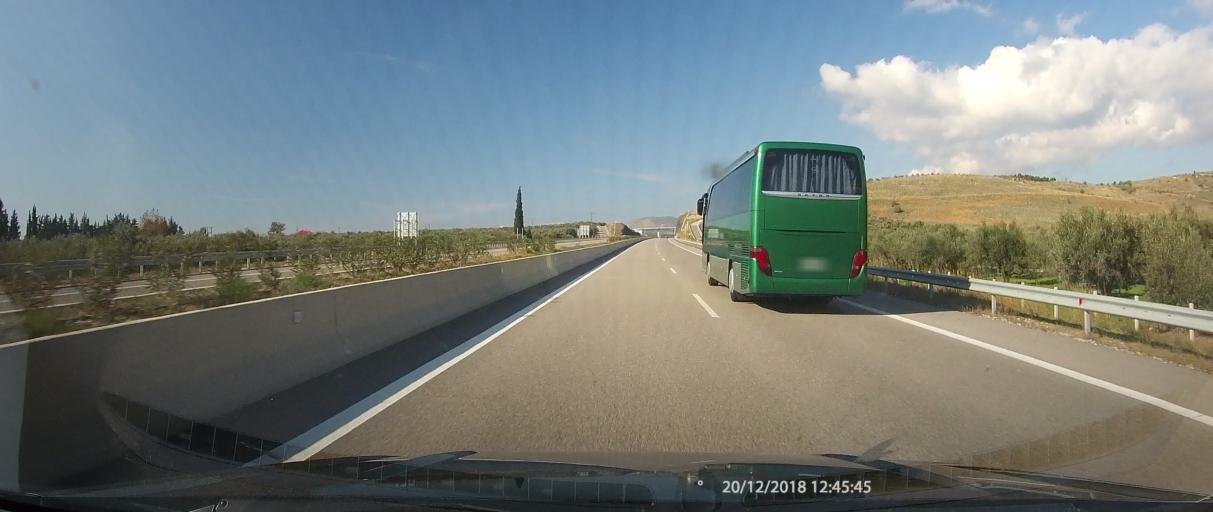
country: GR
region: West Greece
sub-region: Nomos Aitolias kai Akarnanias
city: Mesolongi
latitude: 38.3841
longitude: 21.4885
